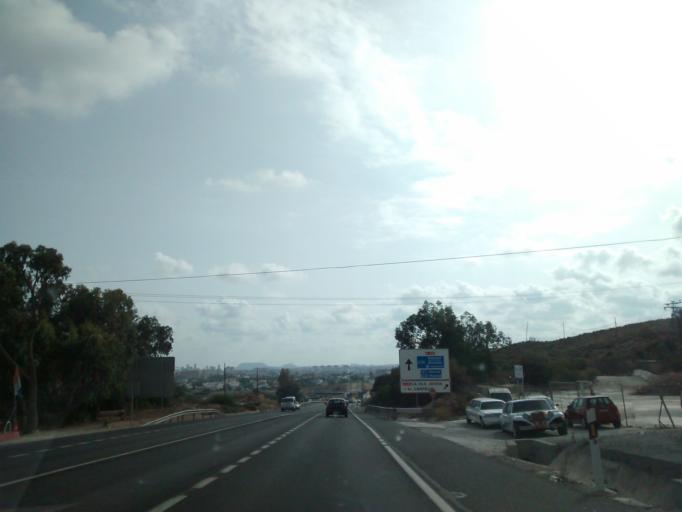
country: ES
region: Valencia
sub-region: Provincia de Alicante
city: el Campello
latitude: 38.4533
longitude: -0.3701
